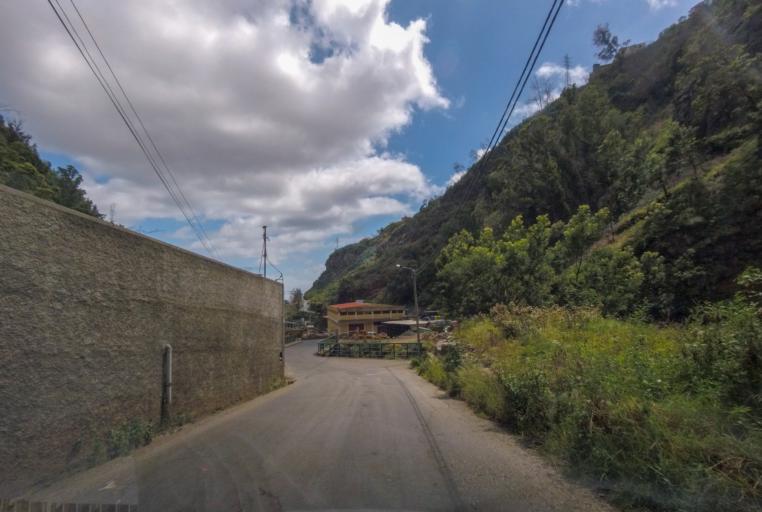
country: PT
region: Madeira
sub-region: Funchal
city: Nossa Senhora do Monte
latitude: 32.6776
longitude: -16.9179
